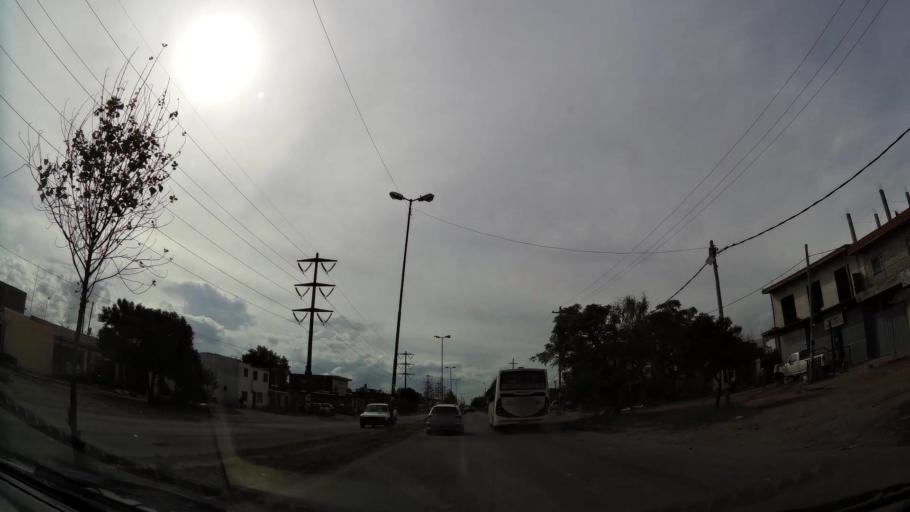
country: AR
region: Buenos Aires
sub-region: Partido de Quilmes
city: Quilmes
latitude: -34.7610
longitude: -58.2538
